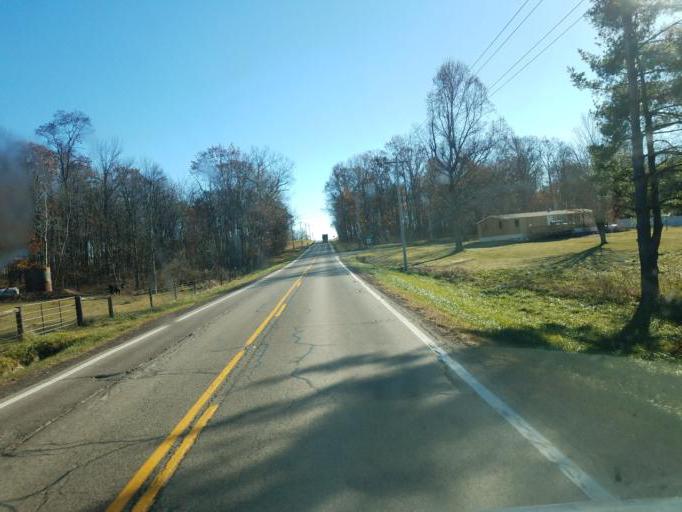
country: US
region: Ohio
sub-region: Knox County
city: Oak Hill
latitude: 40.3381
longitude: -82.2595
